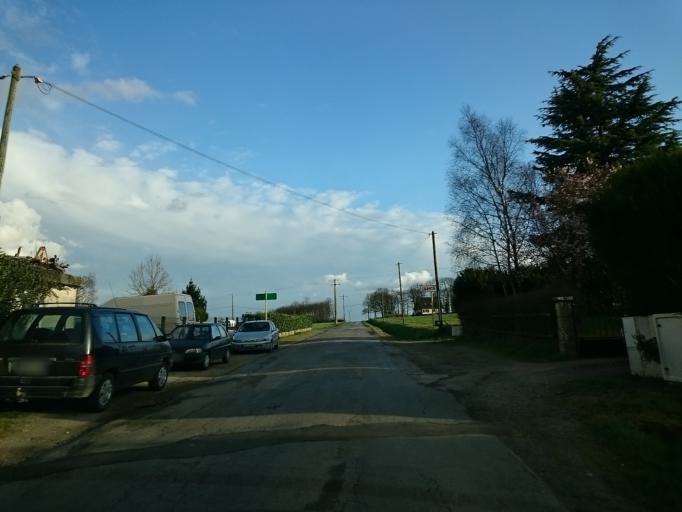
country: FR
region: Brittany
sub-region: Departement d'Ille-et-Vilaine
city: Crevin
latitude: 47.9310
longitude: -1.6615
